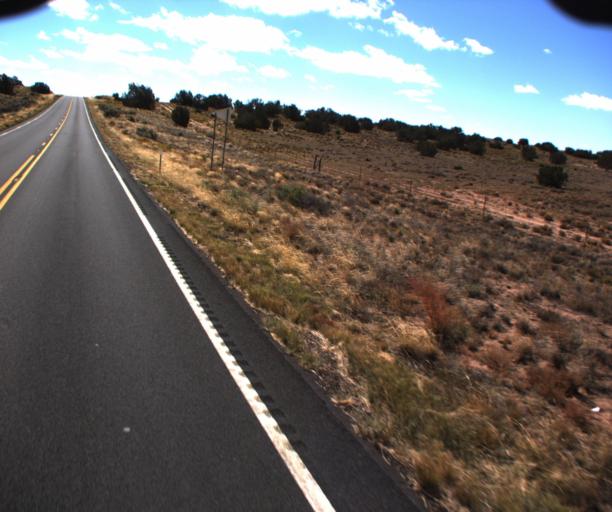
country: US
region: Arizona
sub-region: Apache County
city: Houck
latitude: 35.1216
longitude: -109.3249
